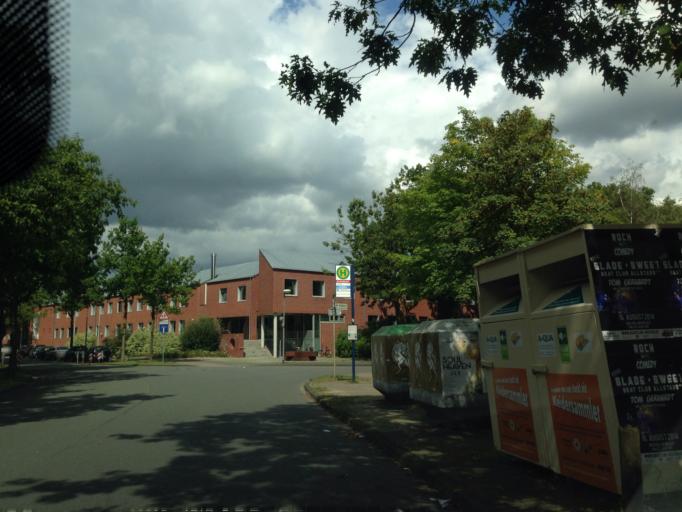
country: DE
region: North Rhine-Westphalia
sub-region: Regierungsbezirk Munster
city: Muenster
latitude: 51.9754
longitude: 7.5744
